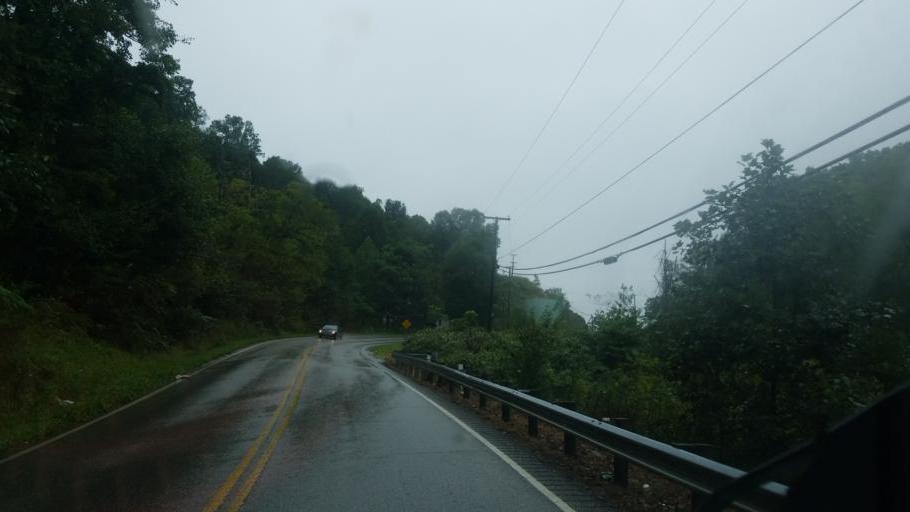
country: US
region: Kentucky
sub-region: Greenup County
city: South Shore
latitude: 38.7122
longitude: -82.9537
